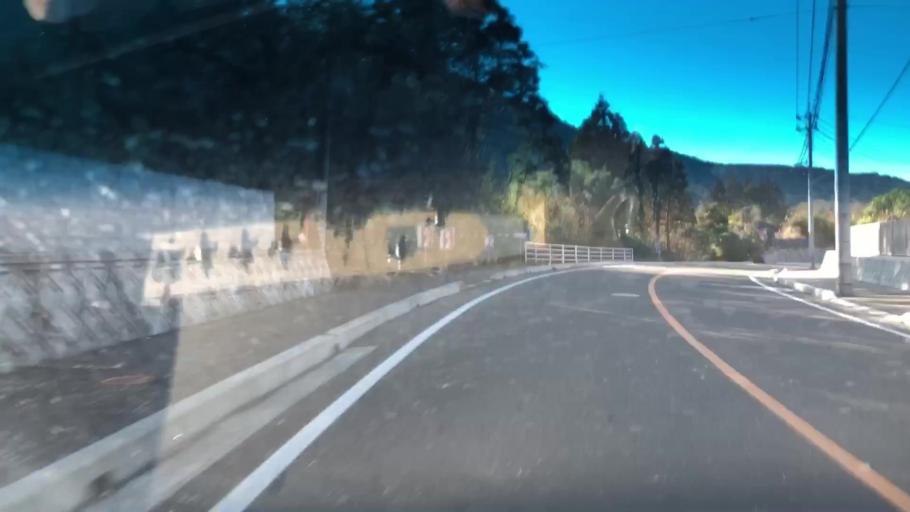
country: JP
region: Kagoshima
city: Satsumasendai
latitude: 31.8162
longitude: 130.2725
